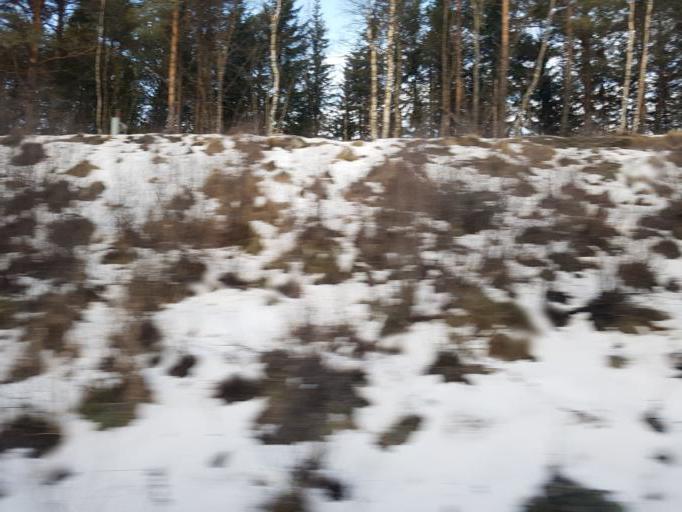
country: NO
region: Sor-Trondelag
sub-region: Rennebu
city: Berkak
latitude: 62.6750
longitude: 9.9150
